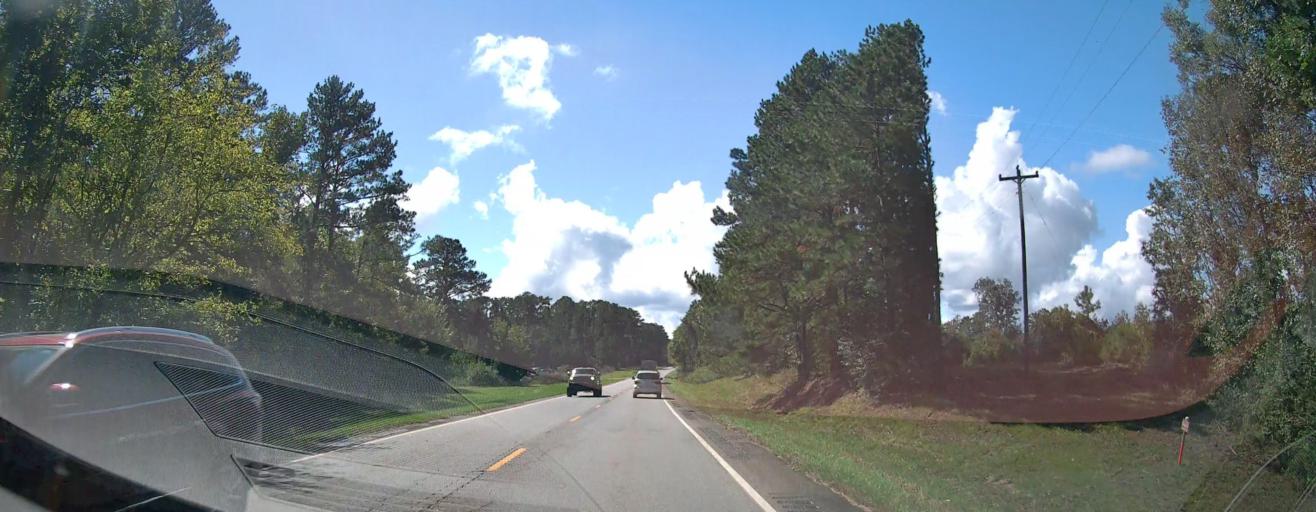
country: US
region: Georgia
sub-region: Jones County
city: Gray
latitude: 33.0398
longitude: -83.4016
